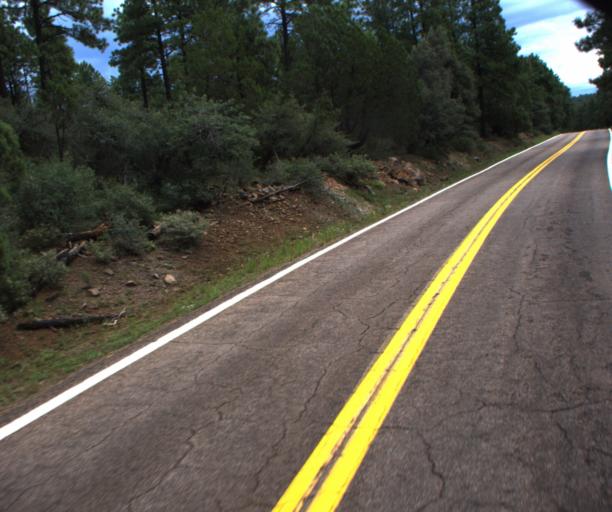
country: US
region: Arizona
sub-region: Greenlee County
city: Morenci
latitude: 33.5015
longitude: -109.3275
